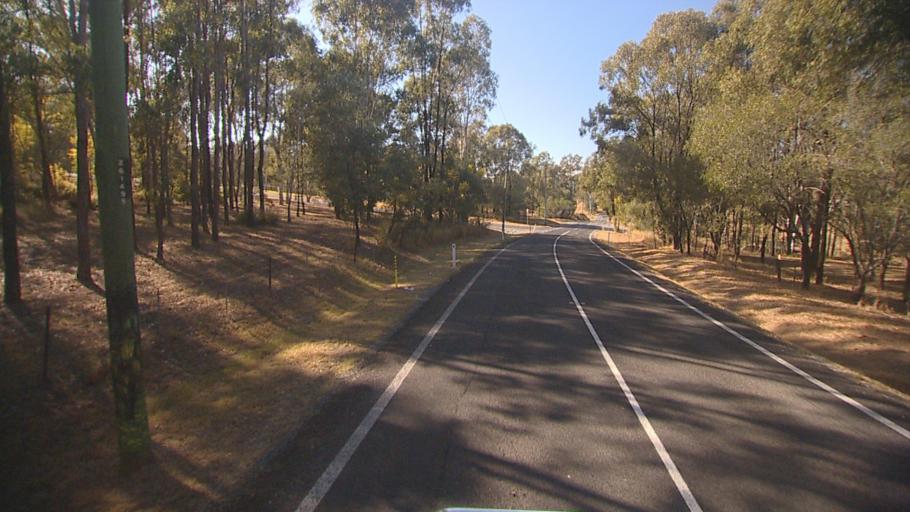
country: AU
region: Queensland
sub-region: Logan
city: Cedar Vale
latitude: -27.8622
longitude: 152.9890
